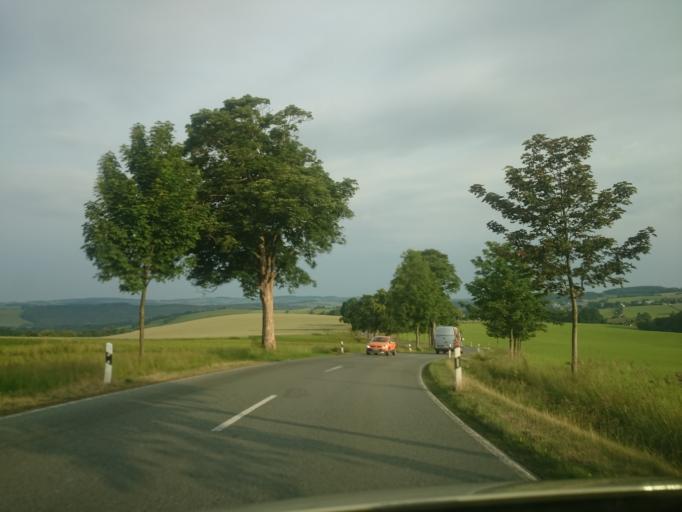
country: DE
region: Saxony
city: Grossolbersdorf
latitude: 50.6845
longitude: 13.1073
